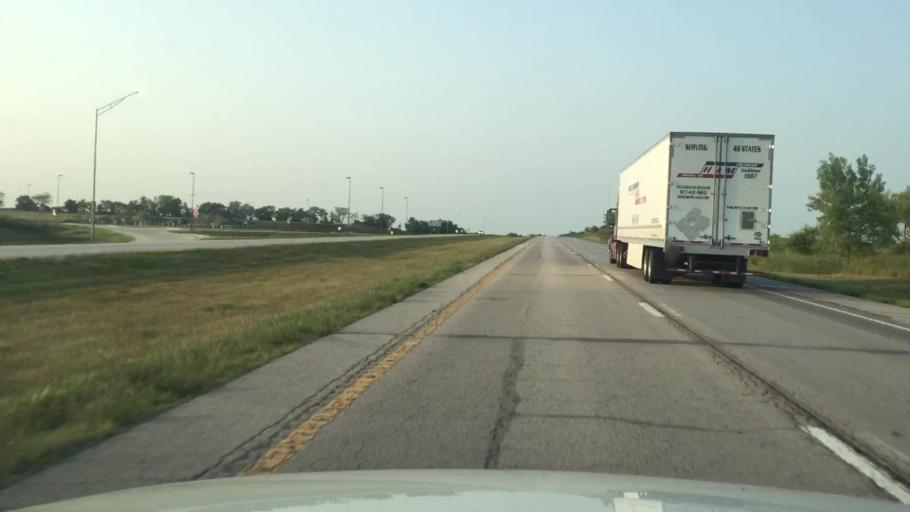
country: US
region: Iowa
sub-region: Decatur County
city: Lamoni
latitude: 40.5469
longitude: -93.9540
